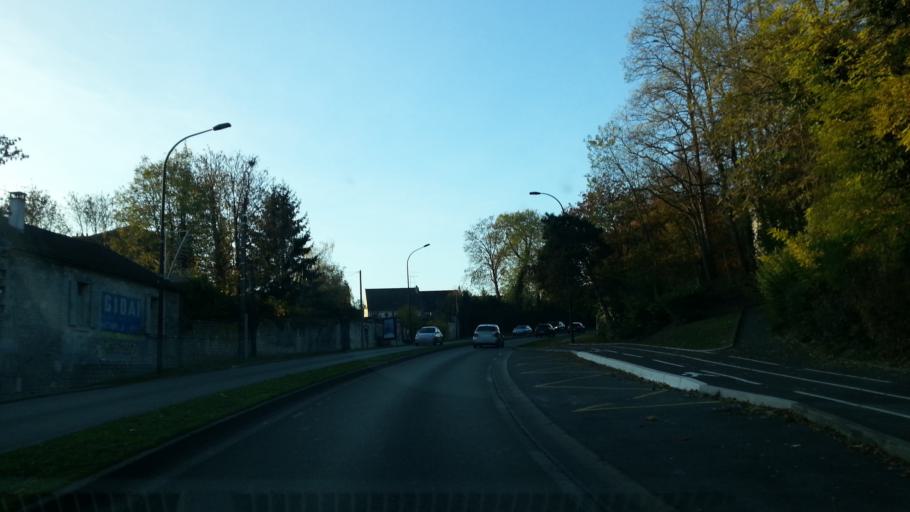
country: FR
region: Picardie
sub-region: Departement de l'Oise
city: Chantilly
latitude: 49.1985
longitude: 2.4626
